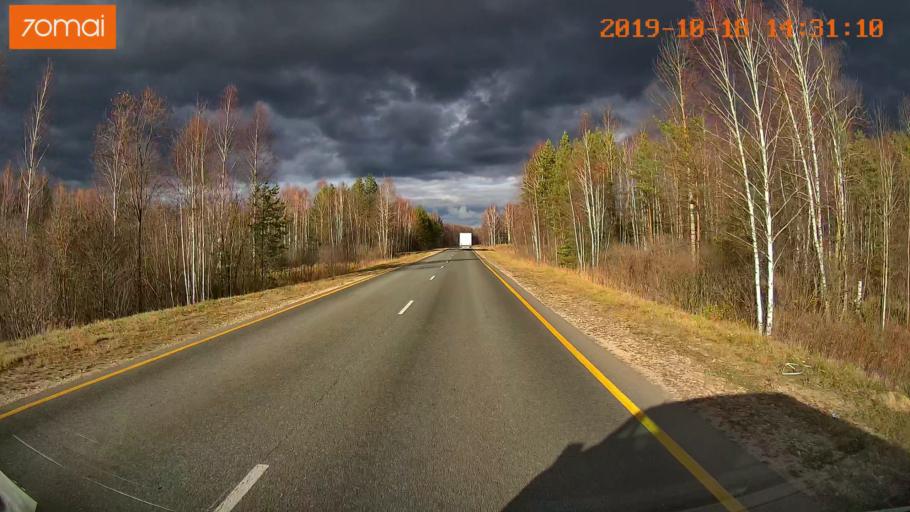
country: RU
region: Rjazan
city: Tuma
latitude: 55.1790
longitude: 40.5686
